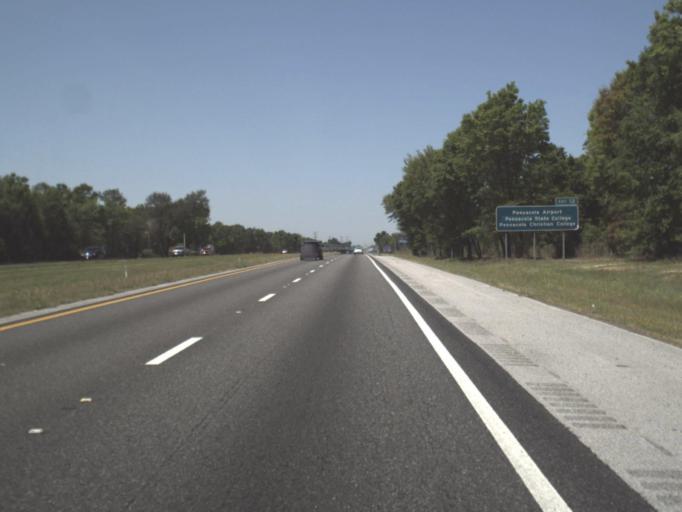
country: US
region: Florida
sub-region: Escambia County
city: Ferry Pass
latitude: 30.5028
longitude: -87.1973
